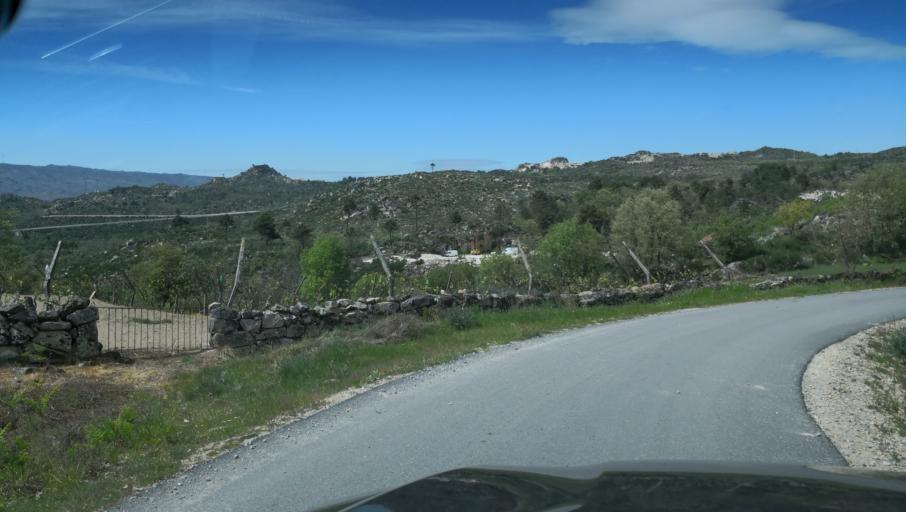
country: PT
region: Vila Real
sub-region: Vila Real
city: Vila Real
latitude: 41.3645
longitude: -7.6702
